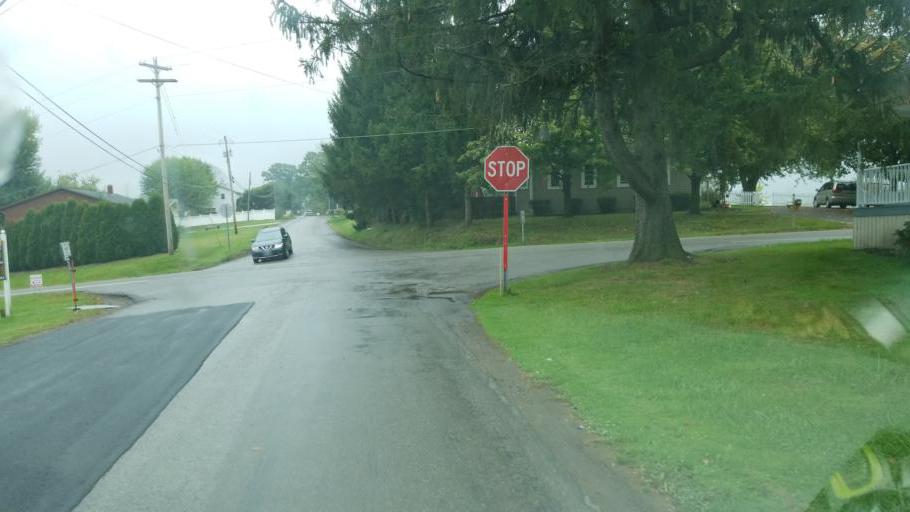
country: US
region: Ohio
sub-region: Tuscarawas County
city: Sugarcreek
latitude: 40.5774
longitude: -81.7112
